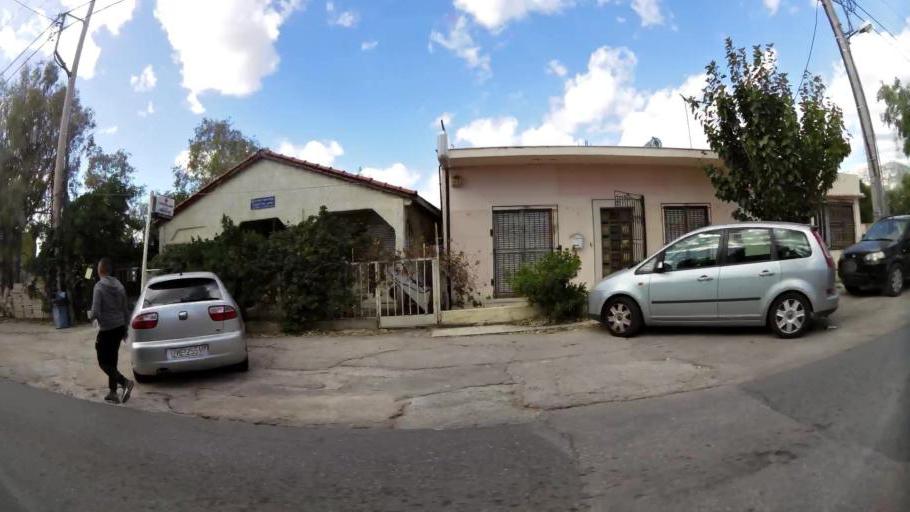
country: GR
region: Attica
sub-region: Nomarchia Anatolikis Attikis
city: Acharnes
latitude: 38.1032
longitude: 23.7424
